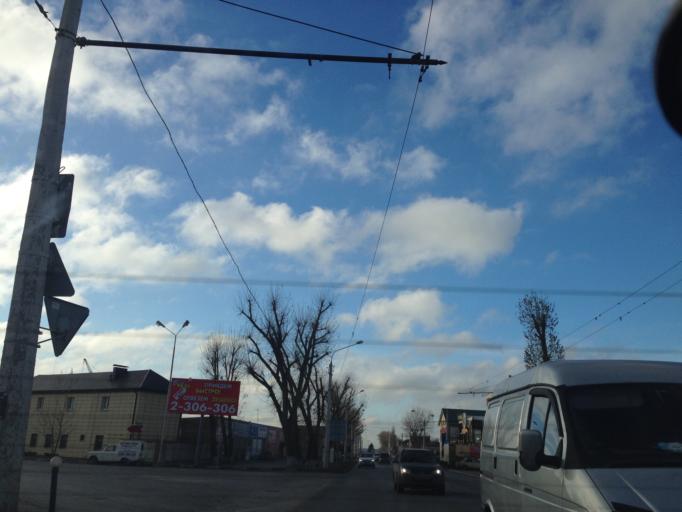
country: RU
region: Rostov
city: Severnyy
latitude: 47.2590
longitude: 39.6279
